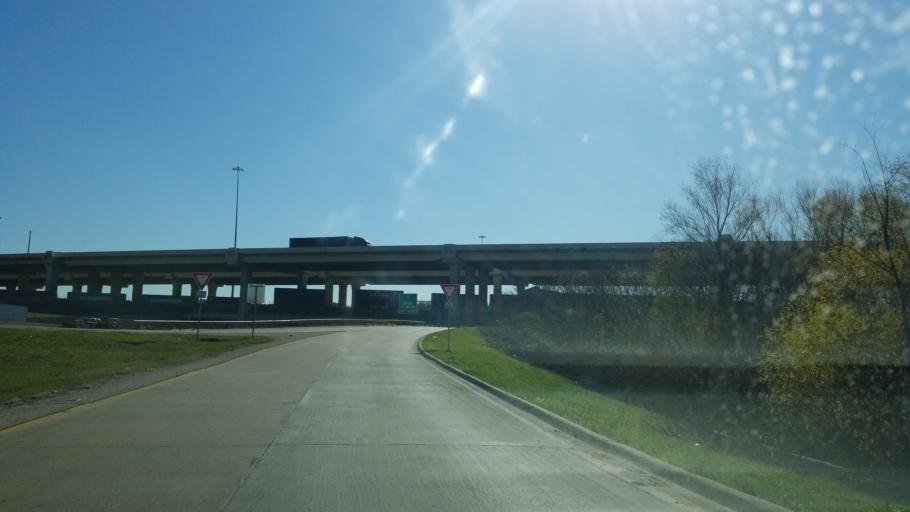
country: US
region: Texas
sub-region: Dallas County
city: Cockrell Hill
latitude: 32.7678
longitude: -96.9158
